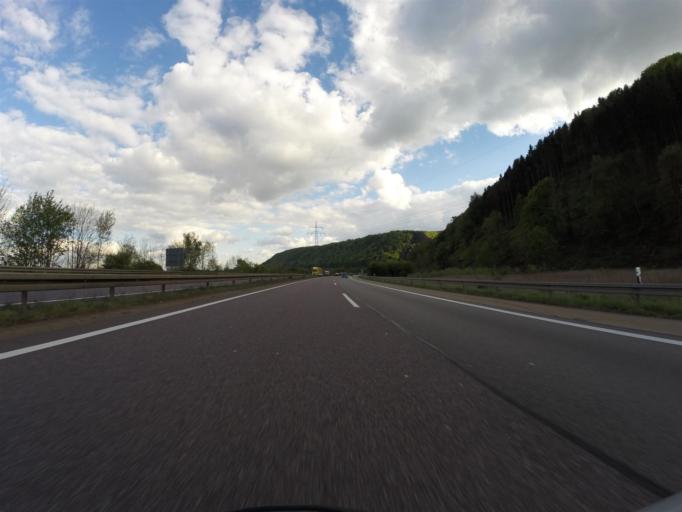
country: DE
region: Saarland
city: Rehlingen-Siersburg
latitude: 49.3541
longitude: 6.7006
